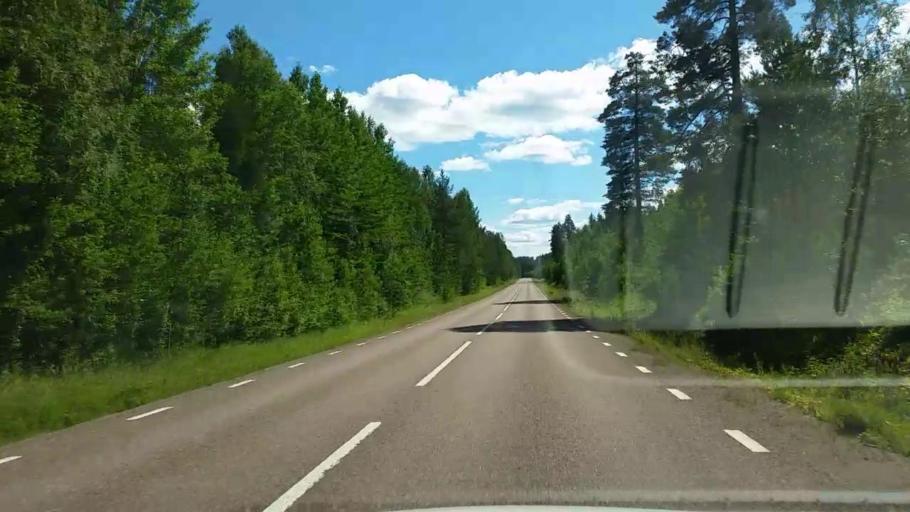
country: SE
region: Dalarna
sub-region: Faluns Kommun
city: Svardsjo
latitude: 60.9685
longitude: 15.6921
